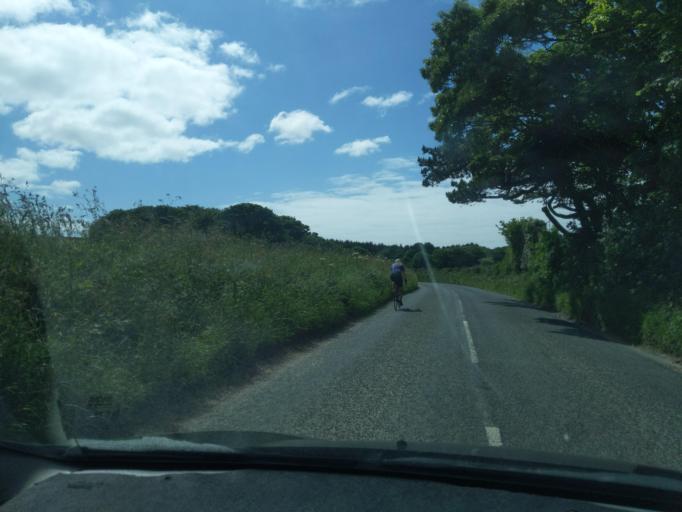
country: GB
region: England
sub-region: Cornwall
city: Perranporth
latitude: 50.2974
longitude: -5.1366
